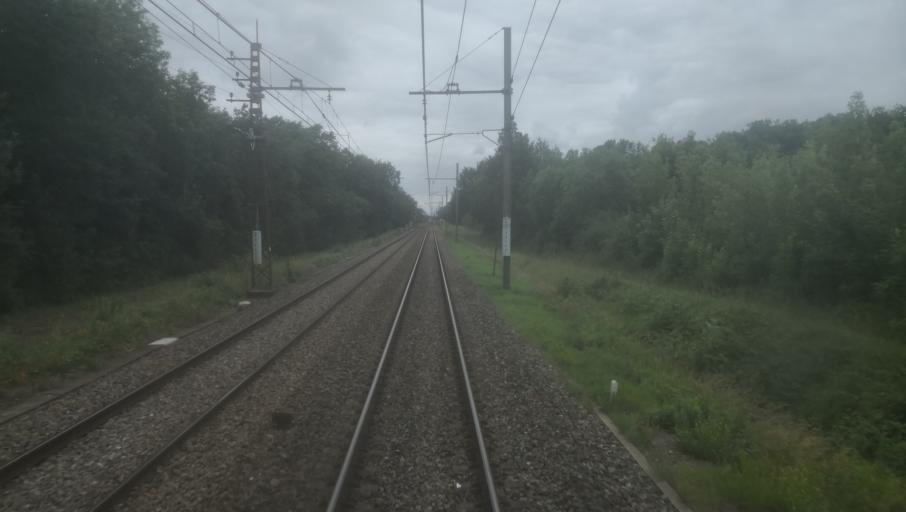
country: FR
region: Midi-Pyrenees
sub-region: Departement du Tarn-et-Garonne
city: Finhan
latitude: 43.8962
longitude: 1.2689
